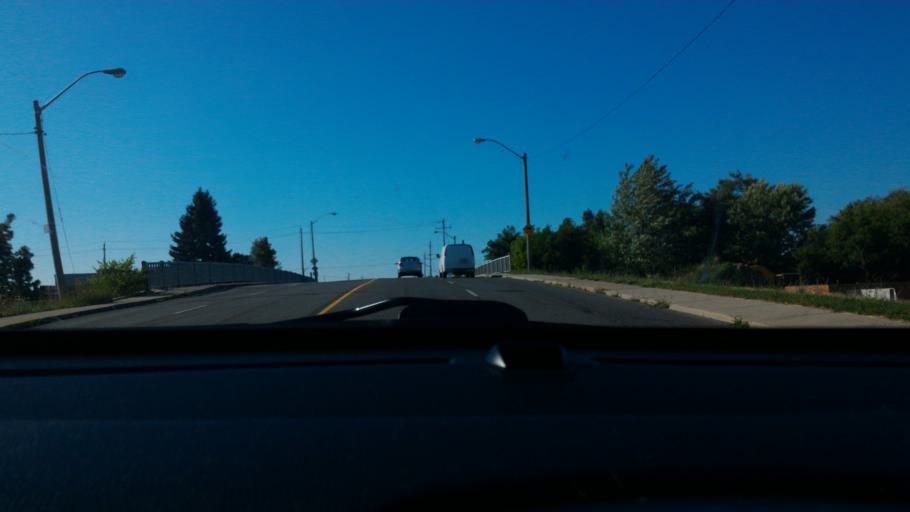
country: CA
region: Ontario
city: Scarborough
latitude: 43.7003
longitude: -79.2653
